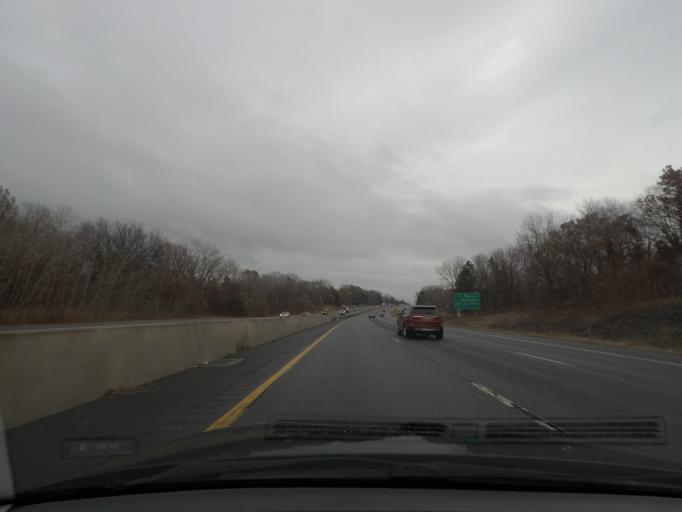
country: US
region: New York
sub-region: Albany County
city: West Albany
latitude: 42.6797
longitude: -73.7686
